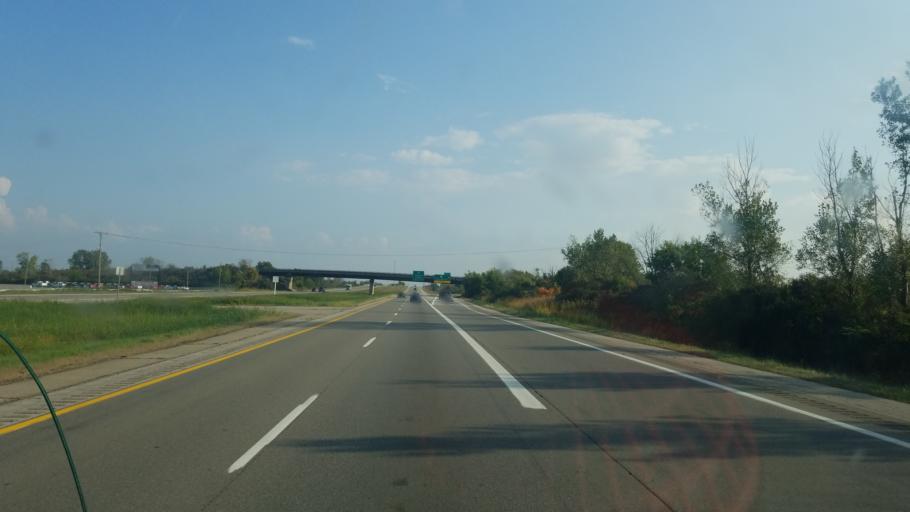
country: US
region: Michigan
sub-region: Monroe County
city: Carleton
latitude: 42.0241
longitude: -83.3517
